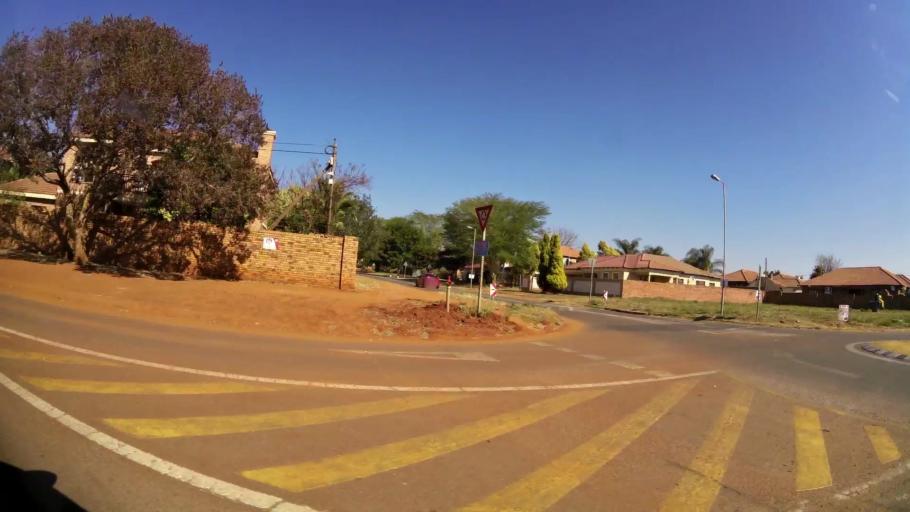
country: ZA
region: Gauteng
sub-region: City of Tshwane Metropolitan Municipality
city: Pretoria
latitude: -25.6614
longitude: 28.2561
